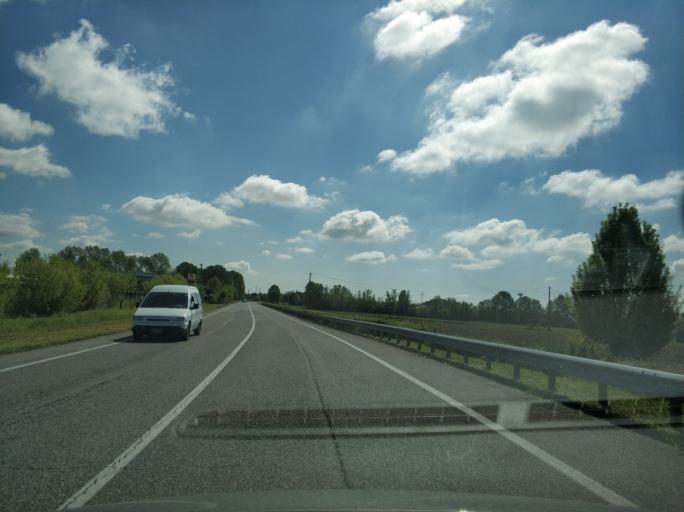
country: IT
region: Veneto
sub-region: Provincia di Venezia
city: Arino
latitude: 45.4321
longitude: 12.0453
